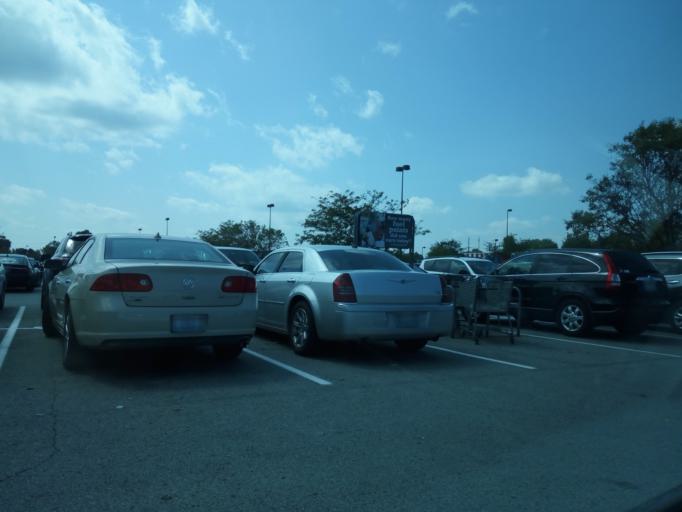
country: US
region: Kentucky
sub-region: Jefferson County
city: Worthington Hills
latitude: 38.2911
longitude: -85.5089
